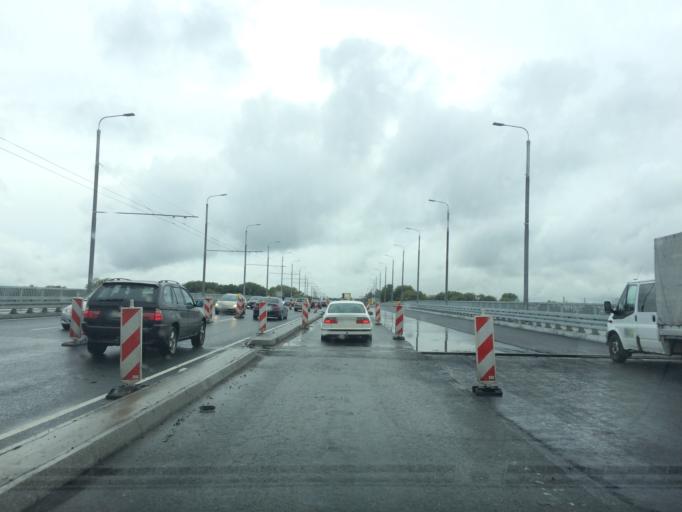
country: LV
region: Riga
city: Riga
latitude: 56.9320
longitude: 24.1186
